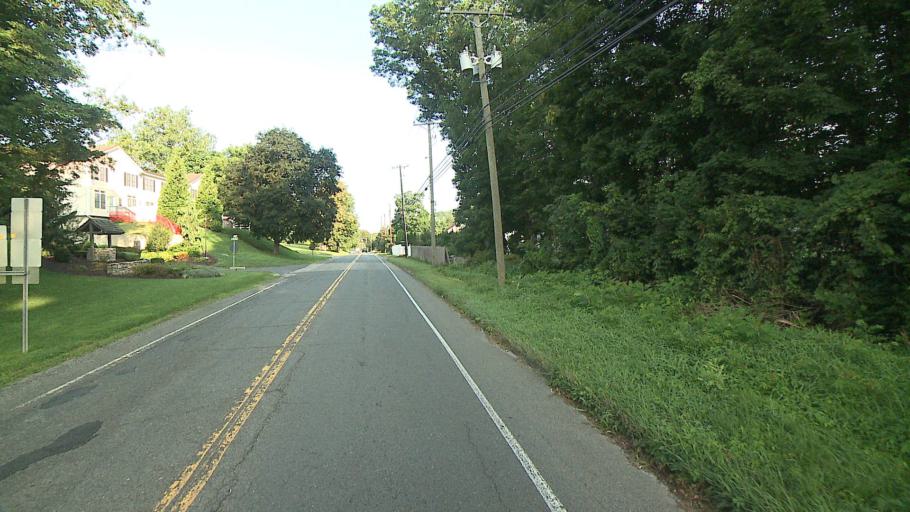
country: US
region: Connecticut
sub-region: Litchfield County
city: New Milford
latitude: 41.5793
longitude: -73.4233
